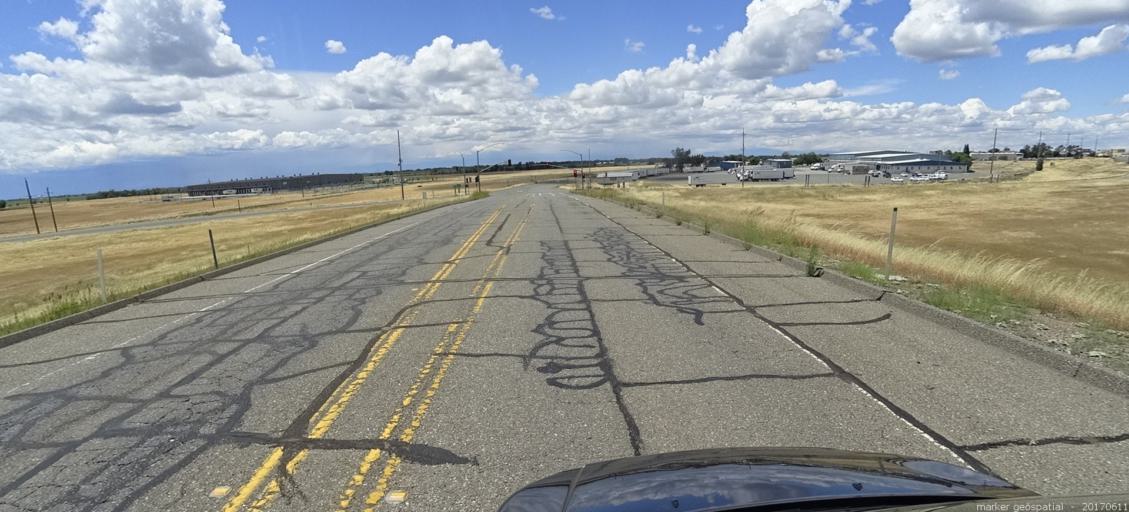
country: US
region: California
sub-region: Butte County
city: Durham
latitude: 39.6423
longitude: -121.7170
